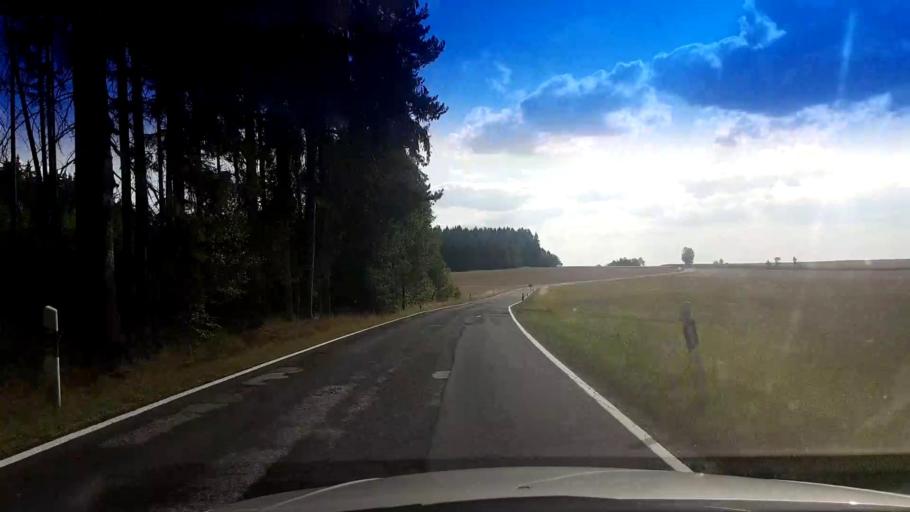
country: DE
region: Bavaria
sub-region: Upper Palatinate
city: Neualbenreuth
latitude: 49.9203
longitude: 12.4036
